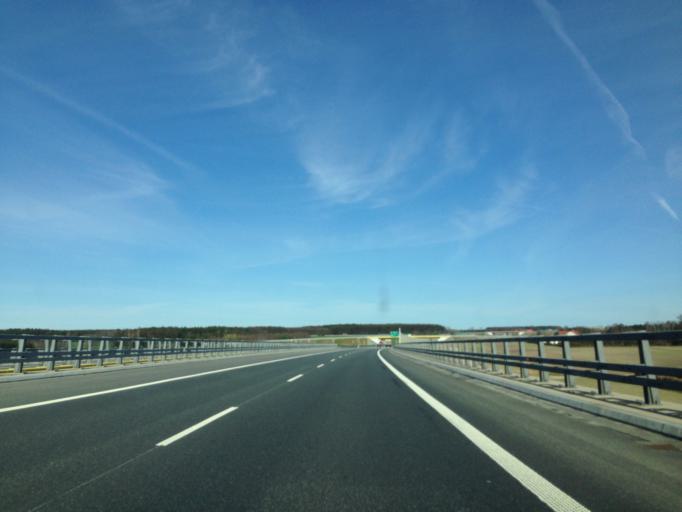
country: PL
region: Lodz Voivodeship
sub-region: Powiat sieradzki
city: Sieradz
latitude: 51.5863
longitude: 18.8061
